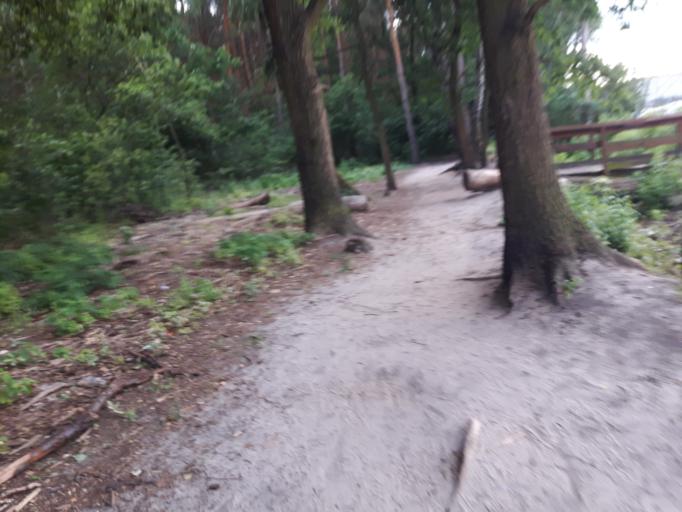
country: PL
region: Masovian Voivodeship
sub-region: Powiat wolominski
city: Zabki
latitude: 52.2776
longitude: 21.1349
